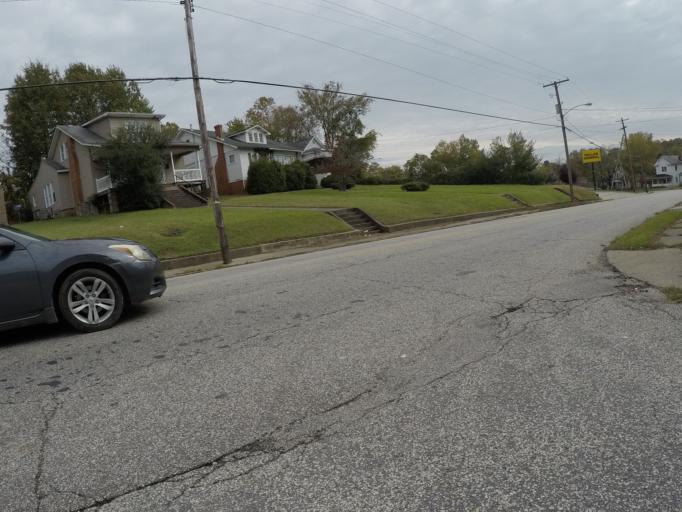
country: US
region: West Virginia
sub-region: Cabell County
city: Huntington
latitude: 38.4079
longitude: -82.4087
